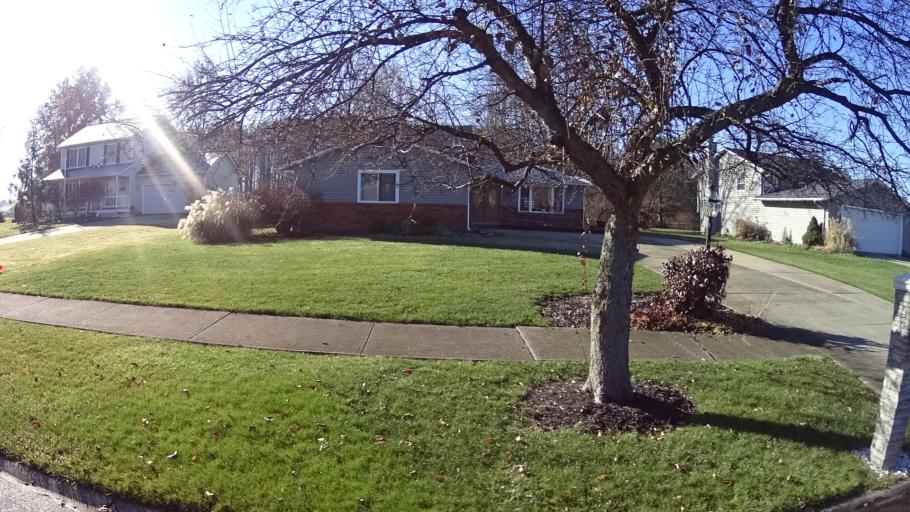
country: US
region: Ohio
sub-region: Lorain County
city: North Ridgeville
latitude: 41.4119
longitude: -82.0120
